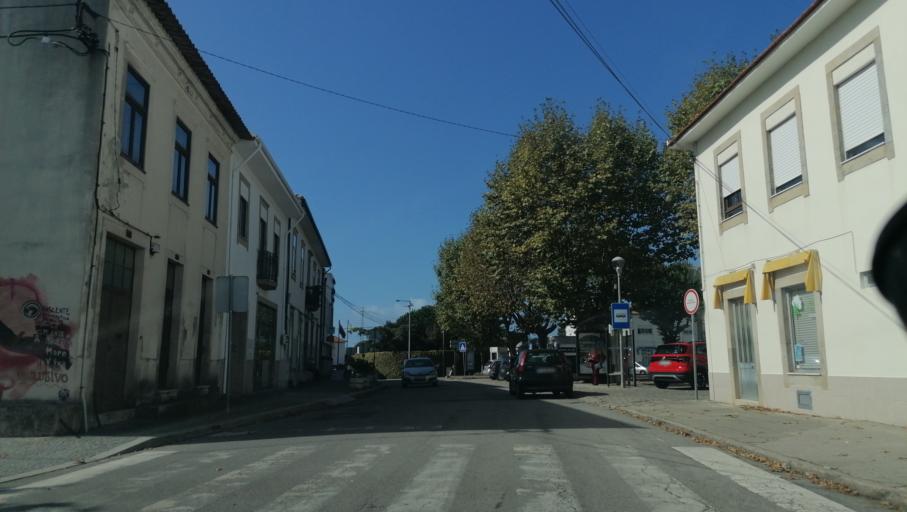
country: PT
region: Aveiro
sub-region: Espinho
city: Silvalde
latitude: 41.0058
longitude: -8.6244
